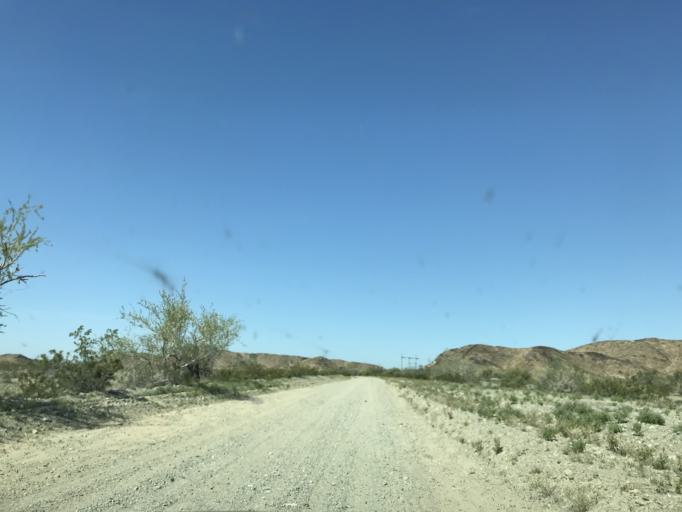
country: US
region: California
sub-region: Riverside County
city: Mesa Verde
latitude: 33.4902
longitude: -114.7826
